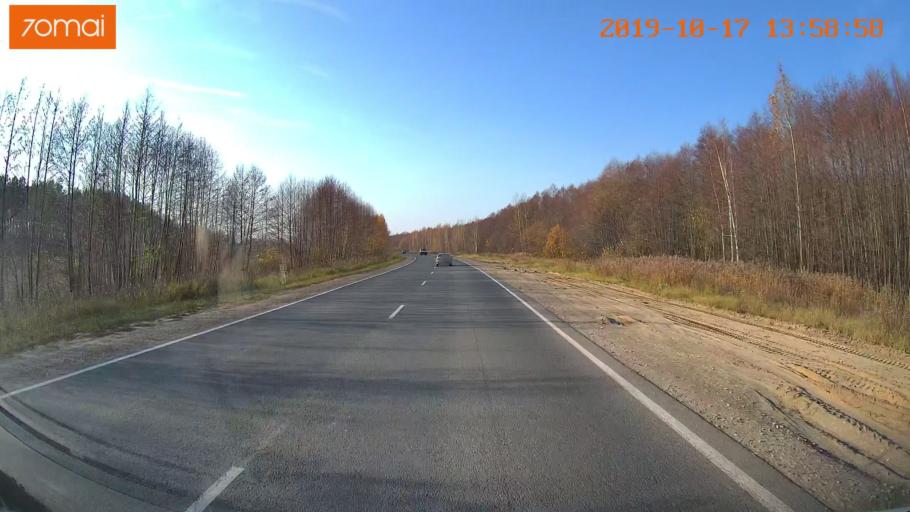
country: RU
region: Rjazan
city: Spas-Klepiki
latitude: 55.1408
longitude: 40.2136
